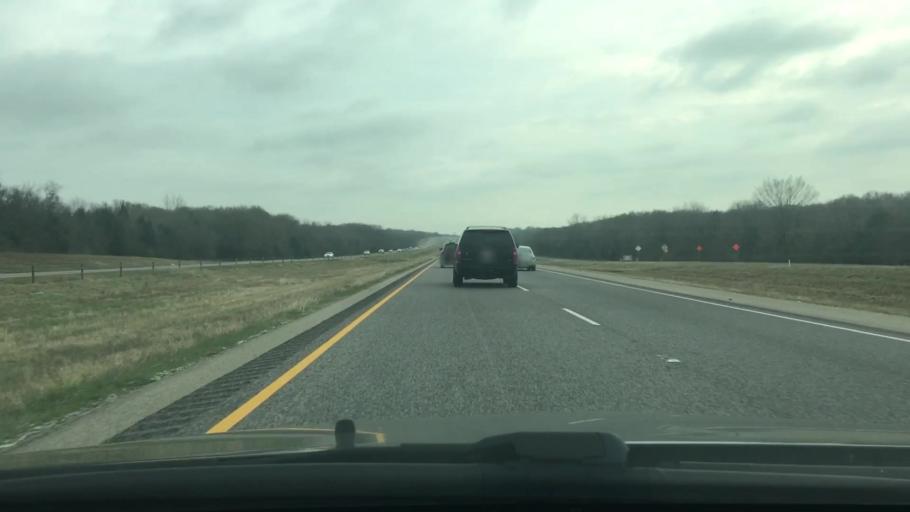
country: US
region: Texas
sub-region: Freestone County
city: Fairfield
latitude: 31.6577
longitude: -96.1614
